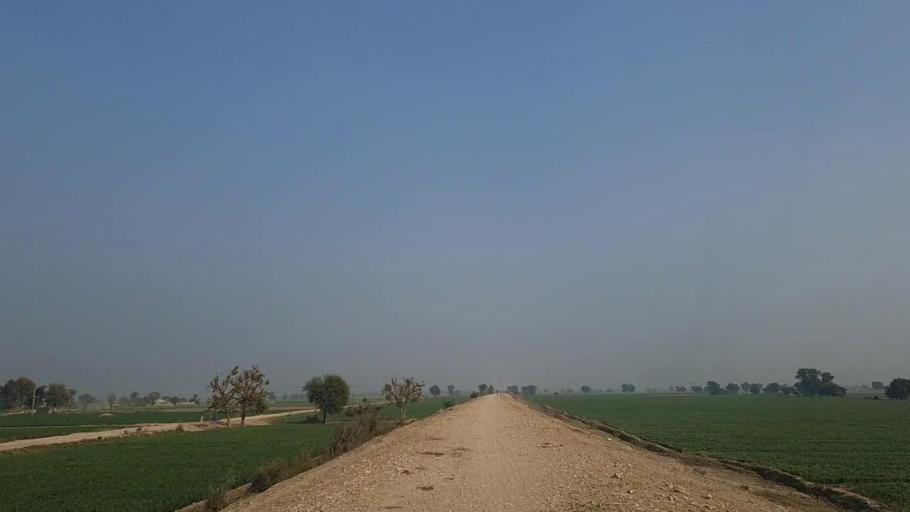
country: PK
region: Sindh
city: Sann
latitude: 26.0863
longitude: 68.1593
